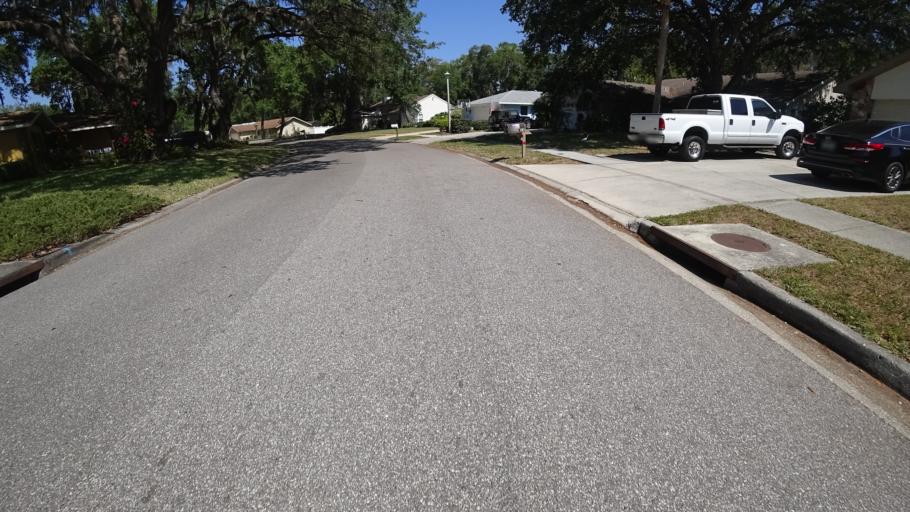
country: US
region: Florida
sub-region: Manatee County
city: Samoset
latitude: 27.4532
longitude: -82.5231
